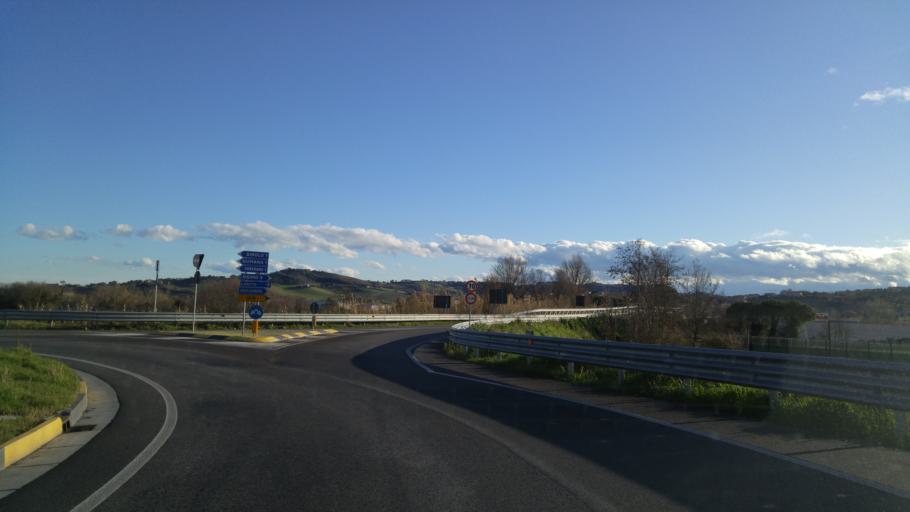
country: IT
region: The Marches
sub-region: Provincia di Ancona
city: Camerano
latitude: 43.5070
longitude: 13.5465
